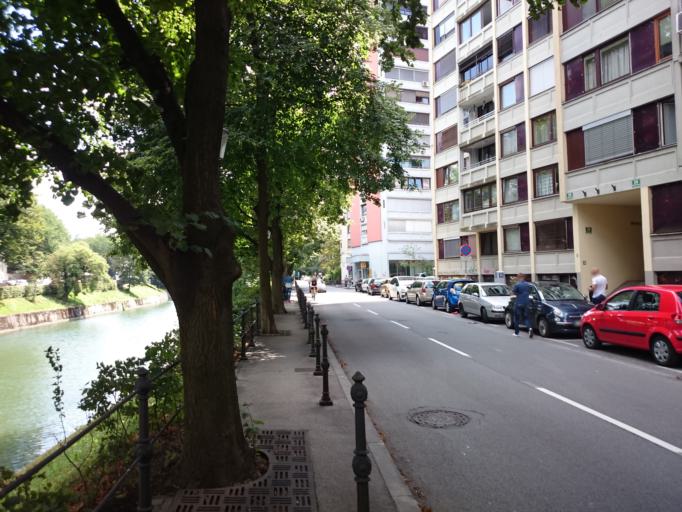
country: SI
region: Ljubljana
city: Ljubljana
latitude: 46.0511
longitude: 14.5143
